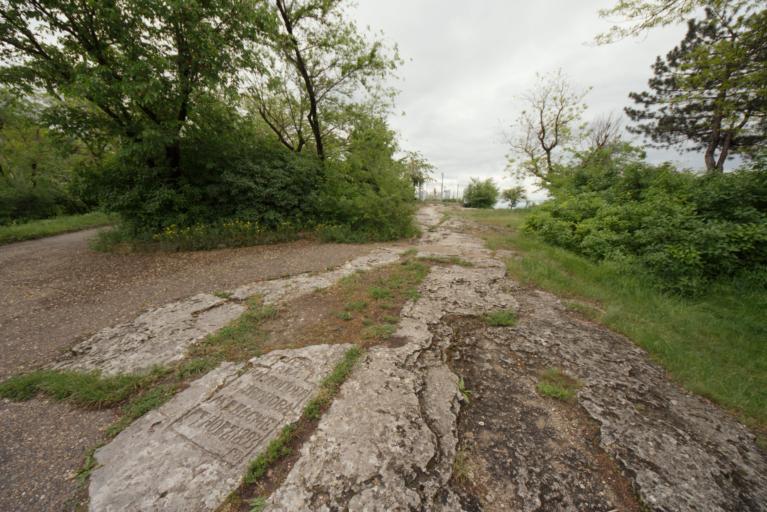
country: RU
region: Stavropol'skiy
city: Goryachevodskiy
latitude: 44.0361
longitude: 43.0842
